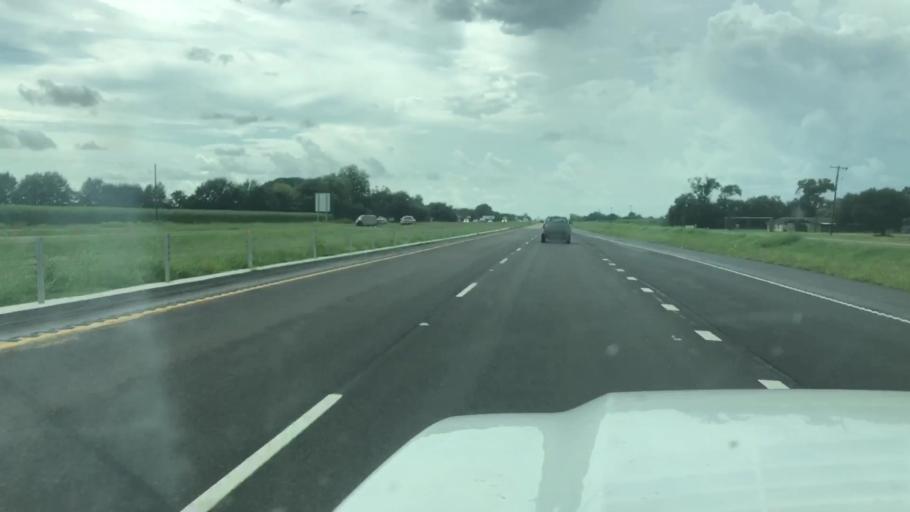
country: US
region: Louisiana
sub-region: Iberia Parish
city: Jeanerette
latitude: 29.8702
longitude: -91.6406
